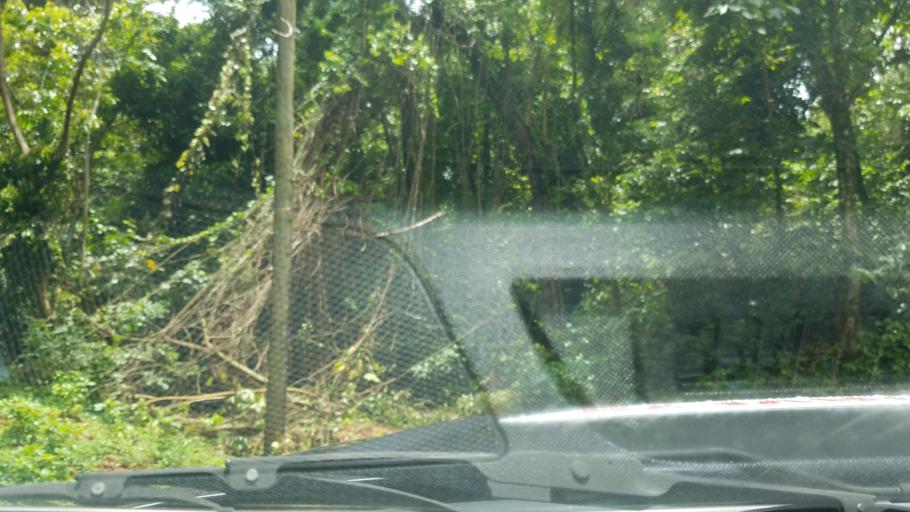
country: LC
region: Castries Quarter
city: Bisee
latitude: 13.9985
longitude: -60.9640
